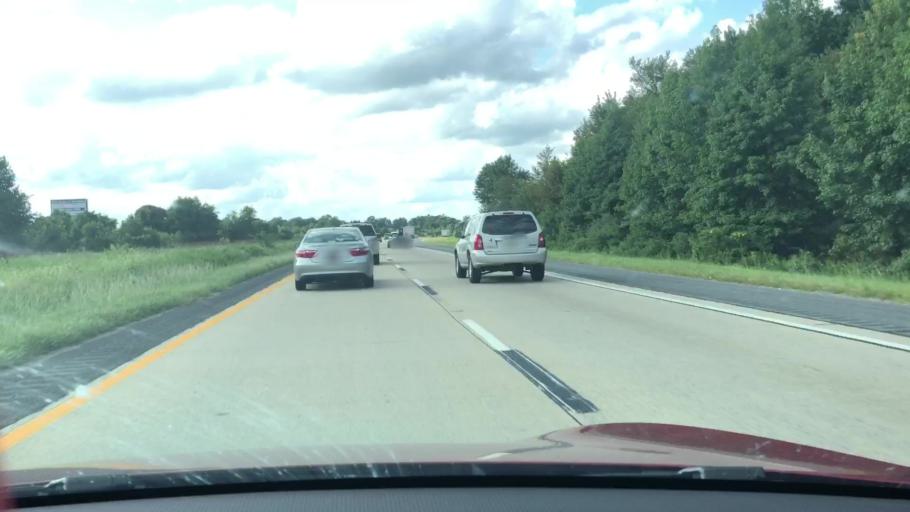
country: US
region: Delaware
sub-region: Kent County
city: Cheswold
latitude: 39.2331
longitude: -75.5829
